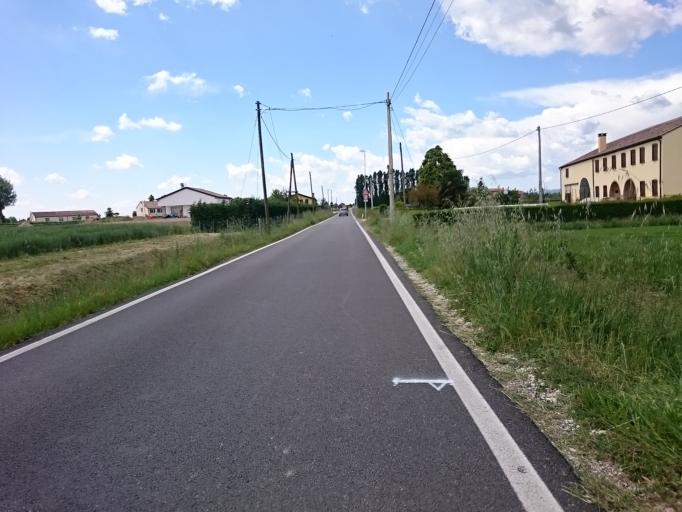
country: IT
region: Veneto
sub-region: Provincia di Padova
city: Casalserugo
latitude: 45.3321
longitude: 11.9310
